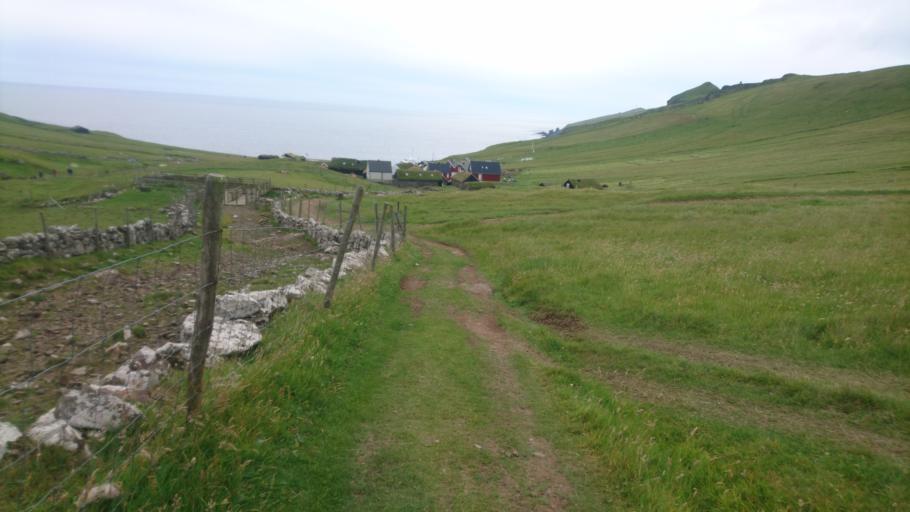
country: FO
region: Vagar
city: Sorvagur
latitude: 62.1055
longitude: -7.6406
